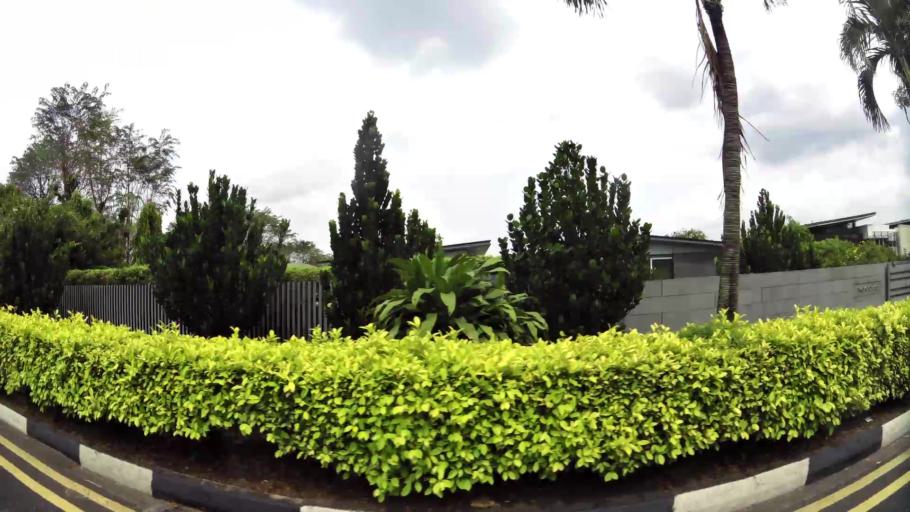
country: SG
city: Singapore
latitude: 1.3172
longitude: 103.7878
